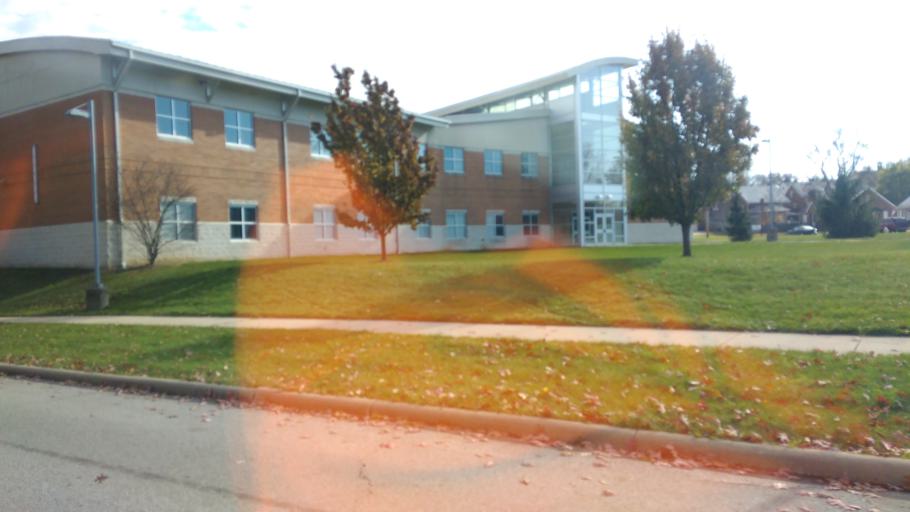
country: US
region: Ohio
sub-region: Richland County
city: Mansfield
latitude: 40.7618
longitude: -82.5455
